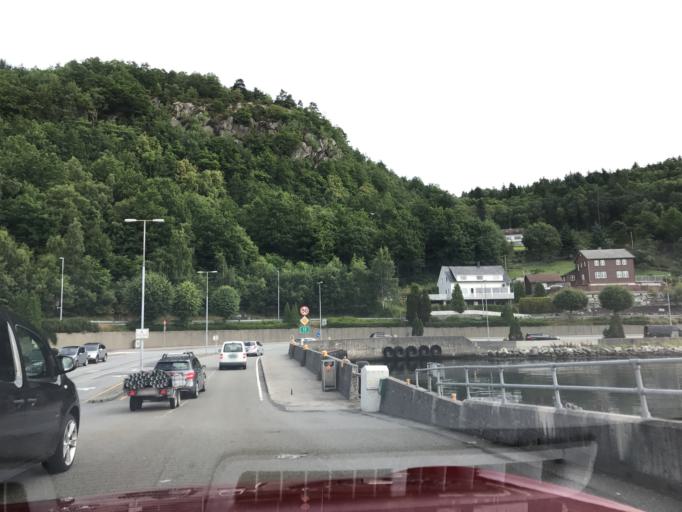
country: NO
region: Rogaland
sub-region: Strand
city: Tau
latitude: 59.0652
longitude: 5.9084
